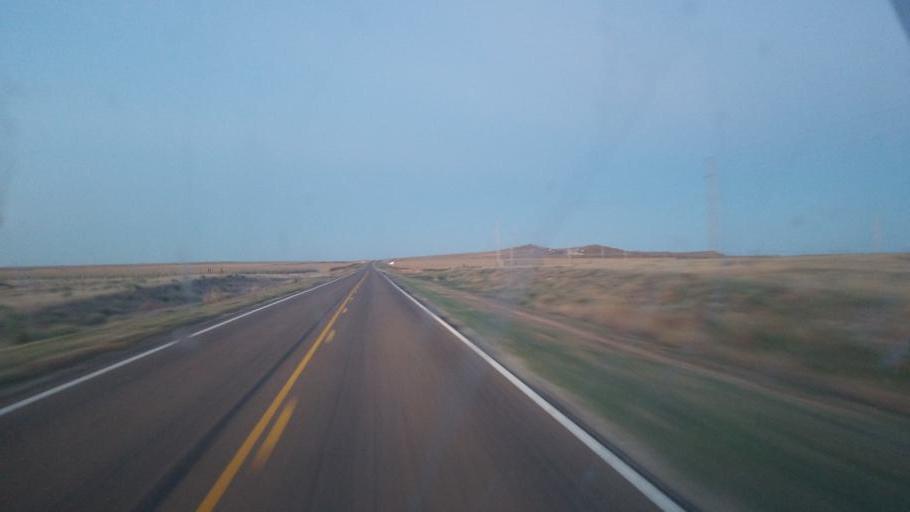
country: US
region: Kansas
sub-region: Wallace County
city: Sharon Springs
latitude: 39.0135
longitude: -101.3579
